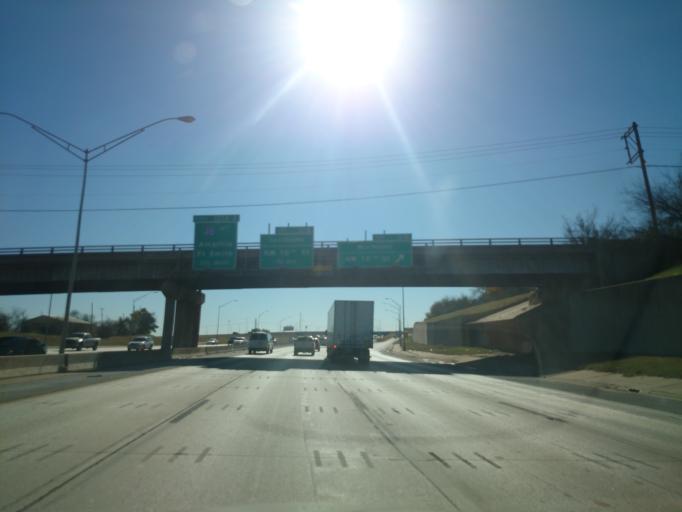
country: US
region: Oklahoma
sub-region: Oklahoma County
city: Warr Acres
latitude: 35.4827
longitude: -97.5786
